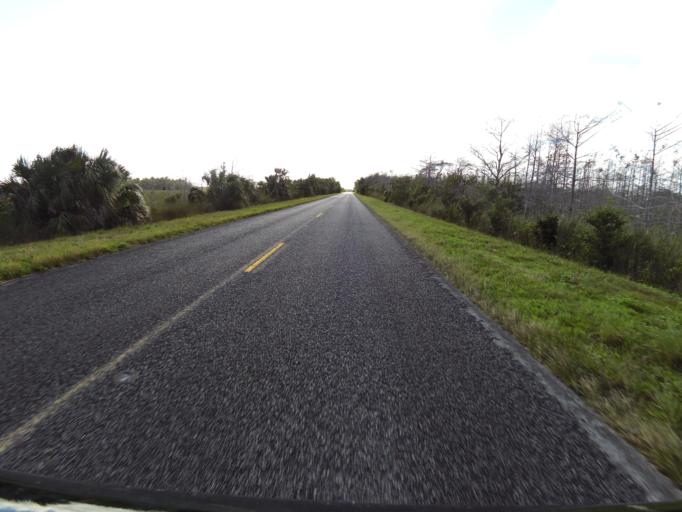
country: US
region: Florida
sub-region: Miami-Dade County
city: Florida City
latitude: 25.4194
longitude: -80.7784
